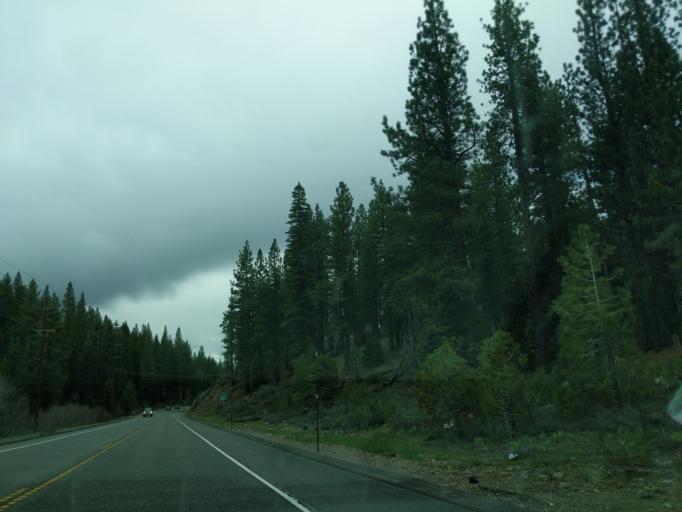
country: US
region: California
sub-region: Placer County
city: Tahoe Vista
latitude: 39.2766
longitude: -120.1027
